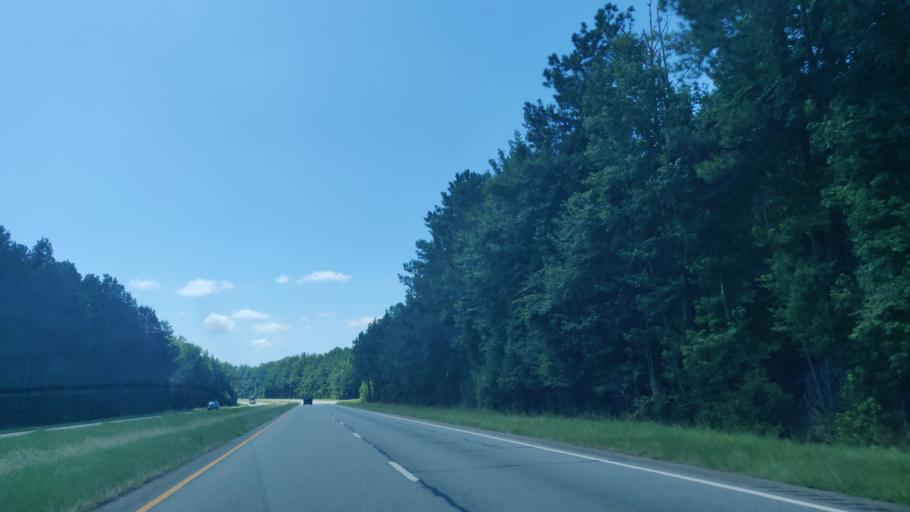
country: US
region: Georgia
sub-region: Chattahoochee County
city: Cusseta
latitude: 32.2789
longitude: -84.7583
